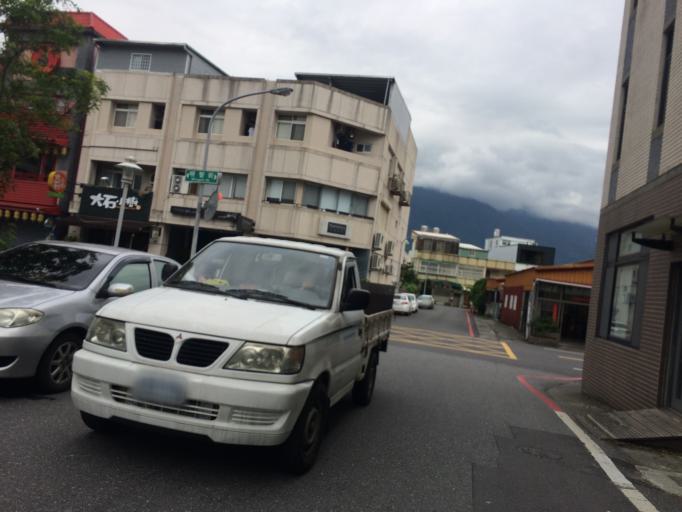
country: TW
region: Taiwan
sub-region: Hualien
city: Hualian
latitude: 23.9854
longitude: 121.6049
